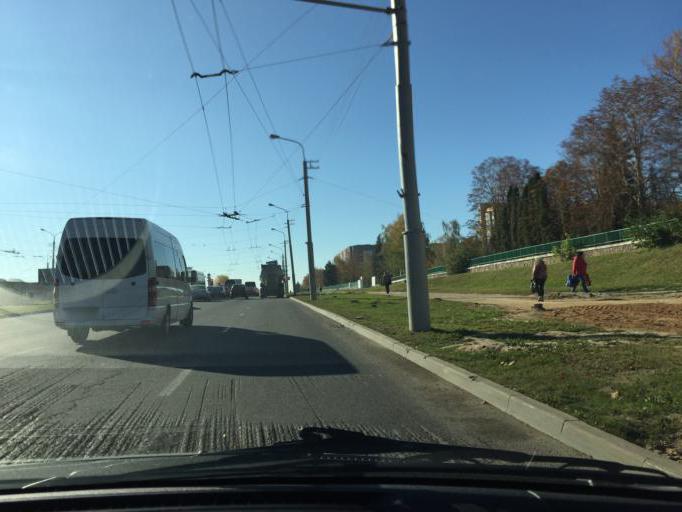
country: BY
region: Minsk
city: Syenitsa
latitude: 53.8516
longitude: 27.5372
